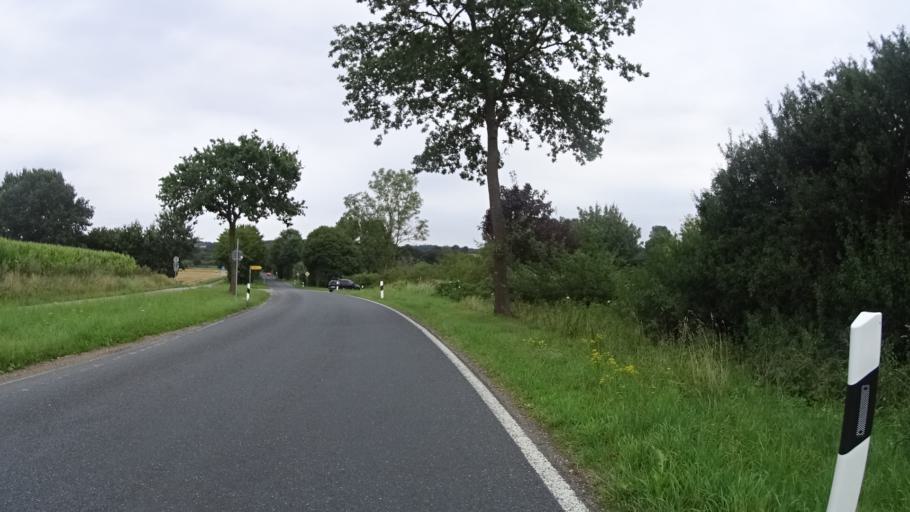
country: DE
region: Schleswig-Holstein
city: Kuhsen
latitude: 53.6834
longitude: 10.6262
